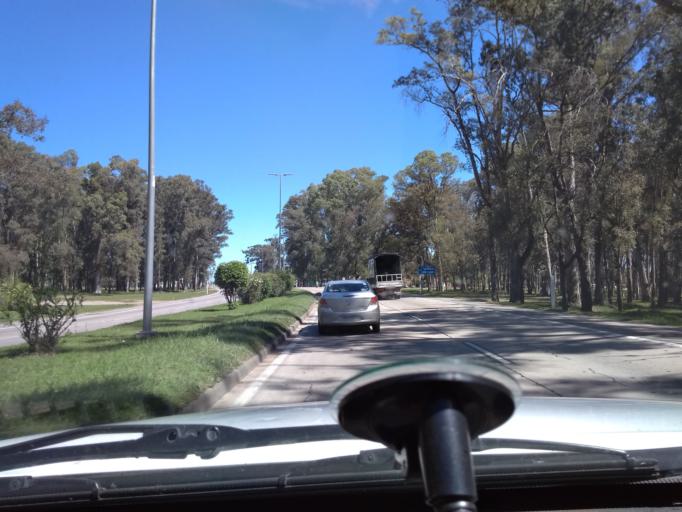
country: UY
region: Canelones
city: Barra de Carrasco
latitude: -34.8571
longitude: -56.0294
